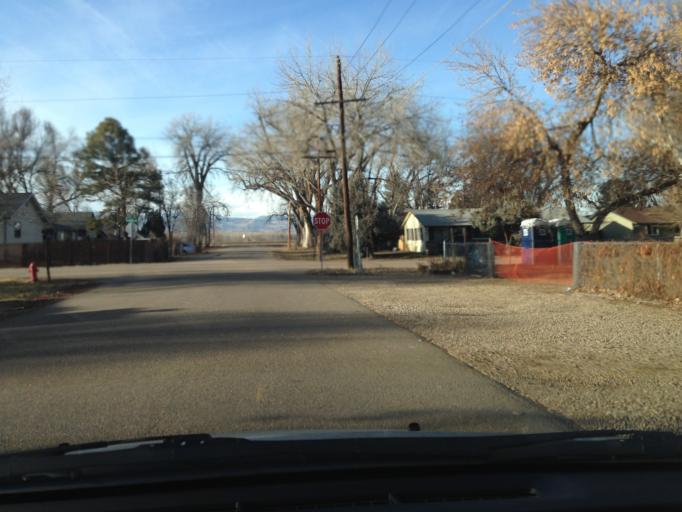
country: US
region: Colorado
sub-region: Boulder County
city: Niwot
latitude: 40.1035
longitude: -105.1706
